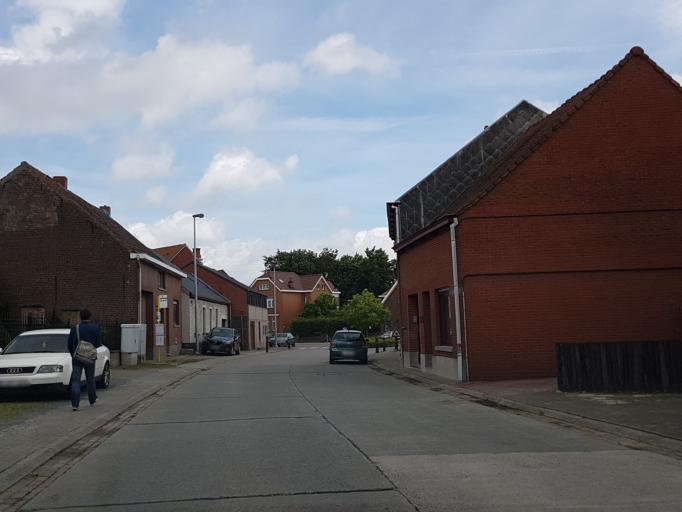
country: BE
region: Flanders
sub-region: Provincie Vlaams-Brabant
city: Ternat
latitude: 50.8960
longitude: 4.1384
